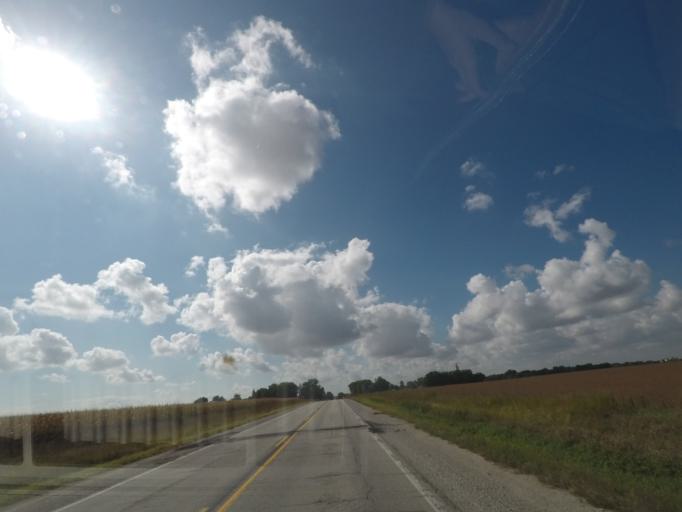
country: US
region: Iowa
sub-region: Story County
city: Nevada
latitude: 42.0277
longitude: -93.3095
